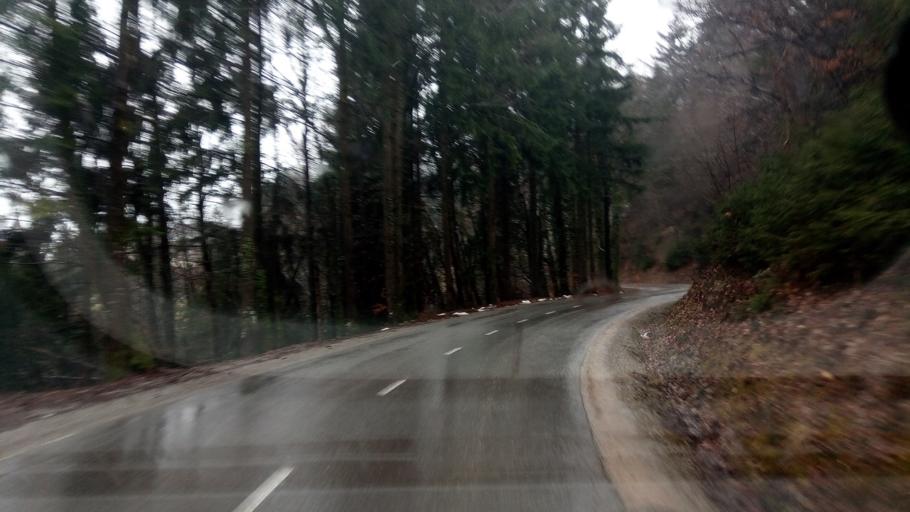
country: SI
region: Ziri
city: Ziri
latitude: 46.0171
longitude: 14.1929
